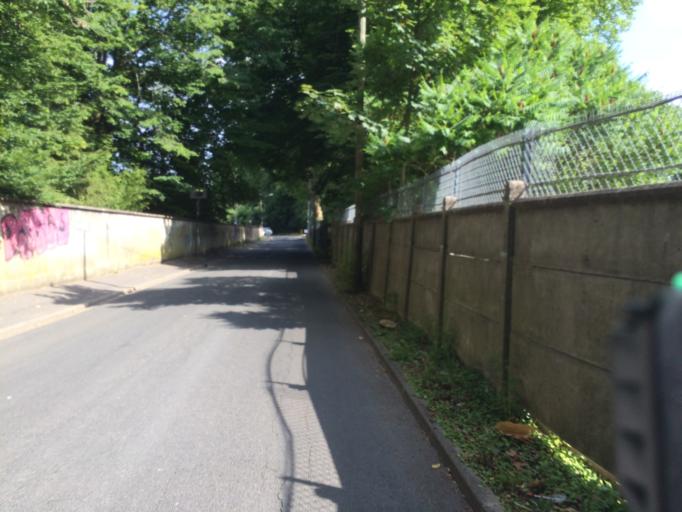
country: FR
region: Ile-de-France
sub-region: Departement de l'Essonne
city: Ris-Orangis
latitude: 48.6599
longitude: 2.4212
